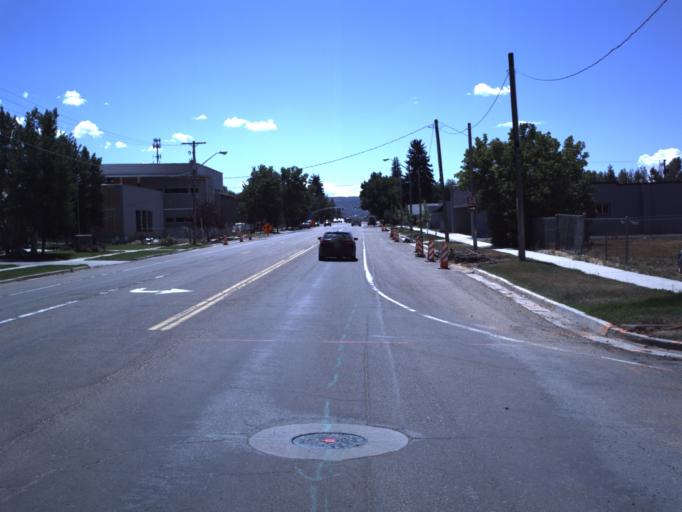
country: US
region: Utah
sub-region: Summit County
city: Kamas
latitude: 40.6464
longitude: -111.2809
